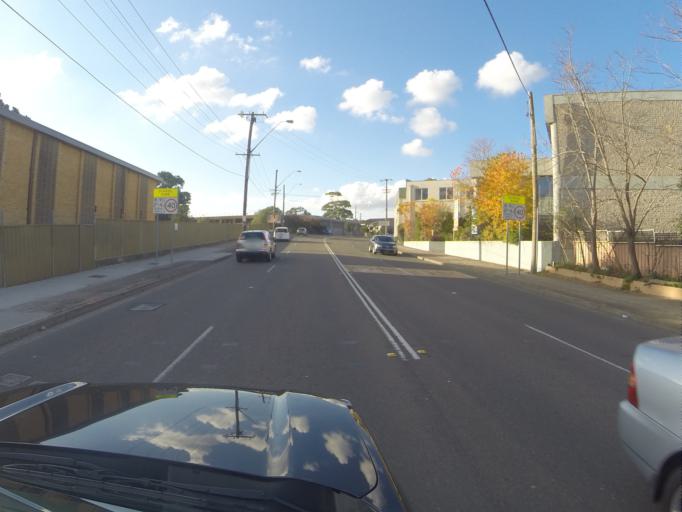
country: AU
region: New South Wales
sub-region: Rockdale
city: Bexley
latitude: -33.9635
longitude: 151.1119
